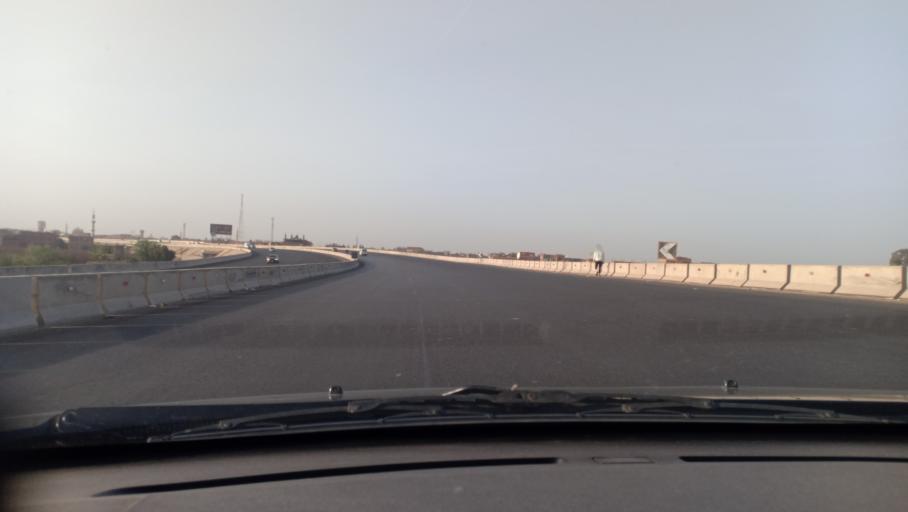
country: EG
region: Muhafazat al Qalyubiyah
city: Qalyub
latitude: 30.1664
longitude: 31.2581
